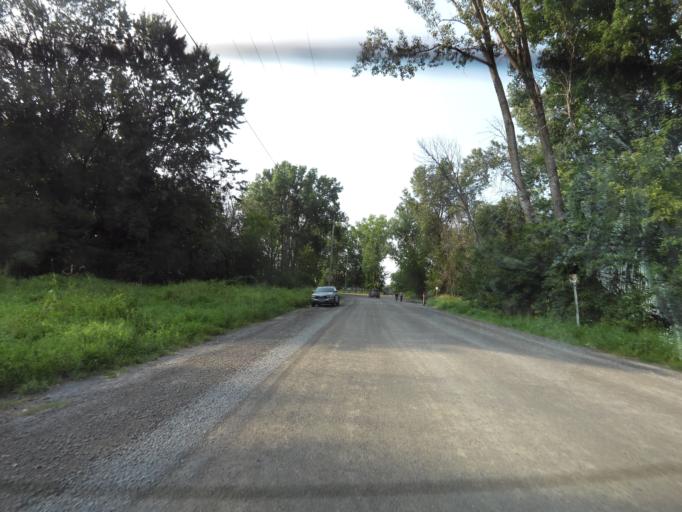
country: CA
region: Ontario
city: Clarence-Rockland
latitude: 45.5041
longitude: -75.4873
